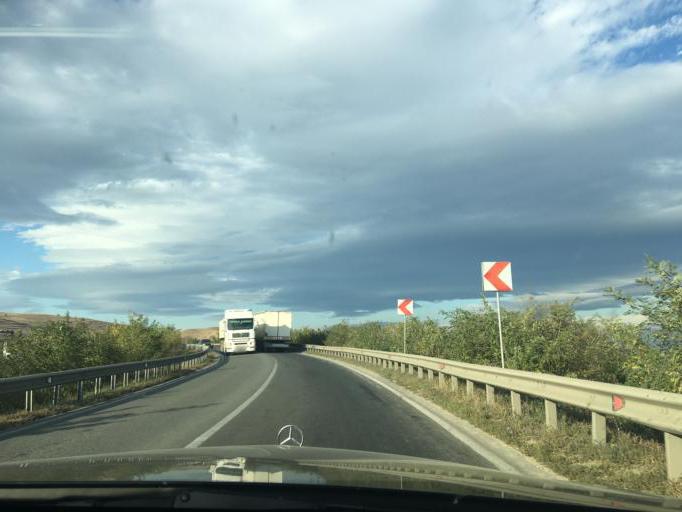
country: RO
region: Alba
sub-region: Municipiul Alba Iulia
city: Barabant
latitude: 46.1026
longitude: 23.6091
